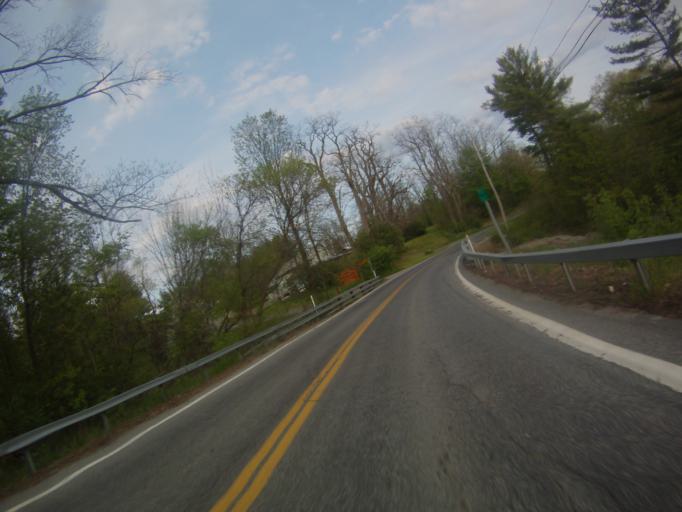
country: US
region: New York
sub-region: Essex County
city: Ticonderoga
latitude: 43.7547
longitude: -73.5080
